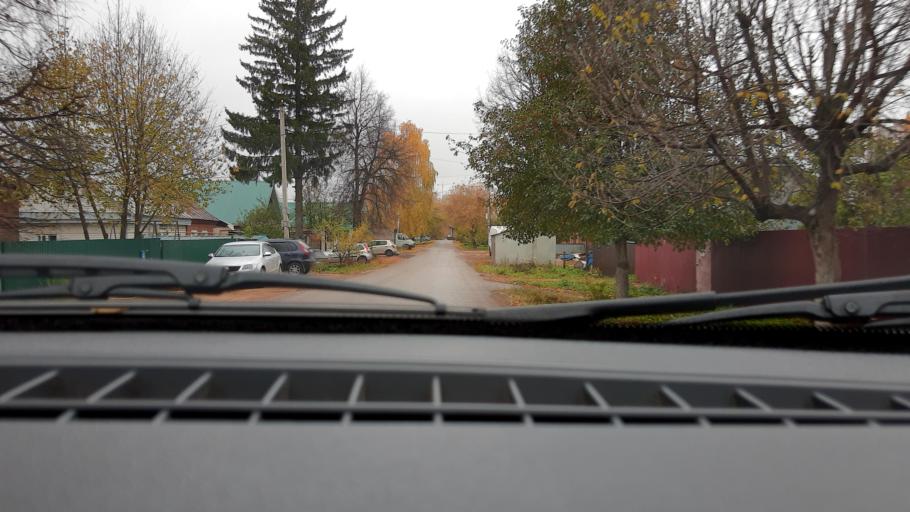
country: RU
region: Bashkortostan
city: Mikhaylovka
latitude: 54.7833
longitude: 55.8919
